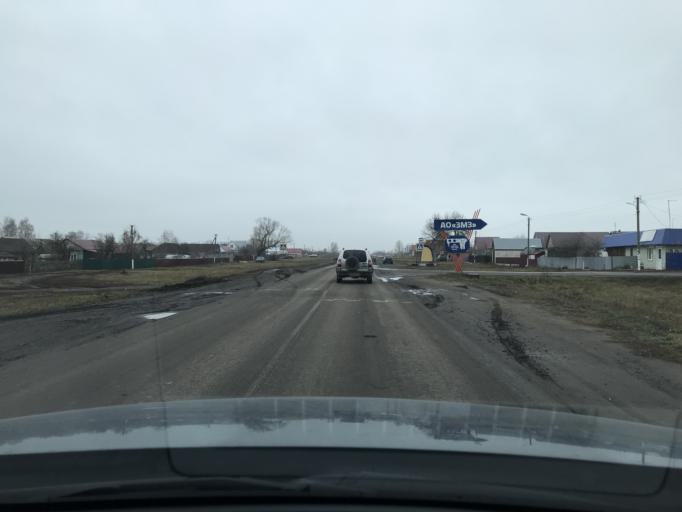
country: RU
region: Penza
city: Zemetchino
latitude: 53.5064
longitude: 42.6359
